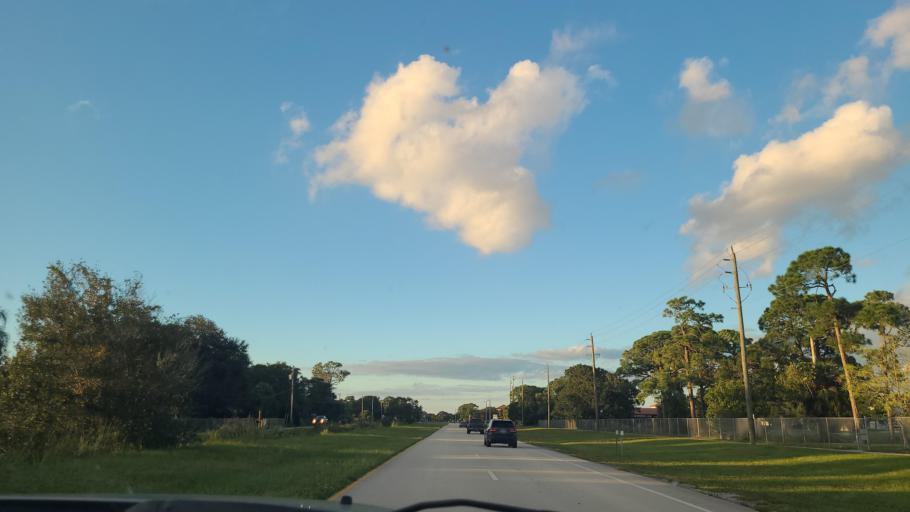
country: US
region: Florida
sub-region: Indian River County
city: Vero Beach South
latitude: 27.6249
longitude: -80.4056
